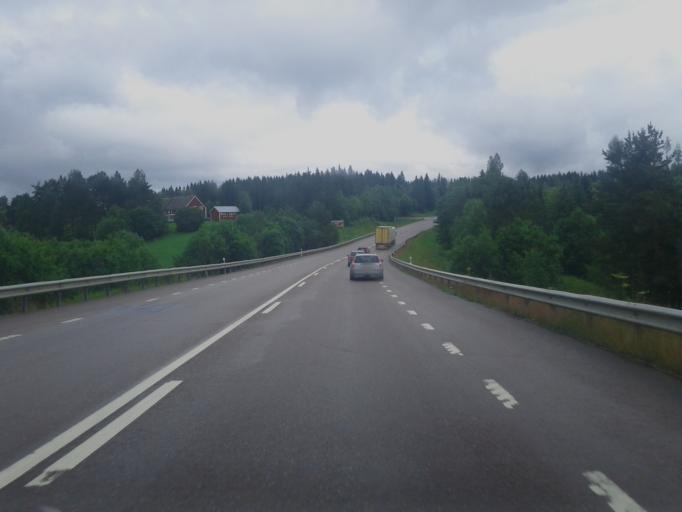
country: SE
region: Vaesternorrland
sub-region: Haernoesands Kommun
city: Haernoesand
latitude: 62.6933
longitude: 17.8522
